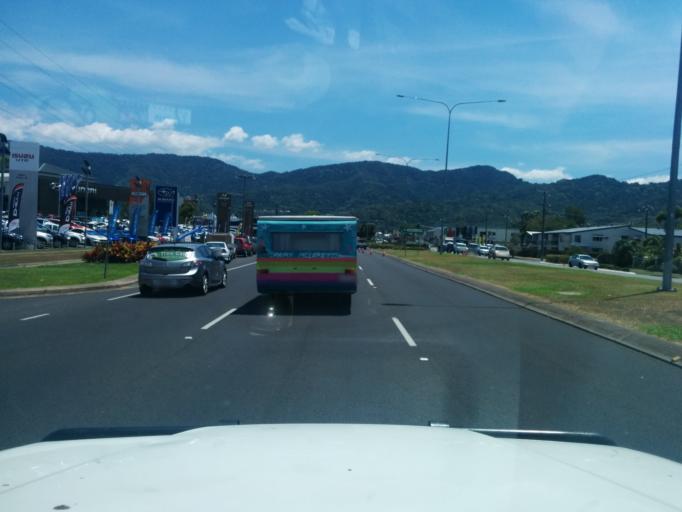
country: AU
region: Queensland
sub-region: Cairns
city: Woree
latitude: -16.9398
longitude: 145.7434
